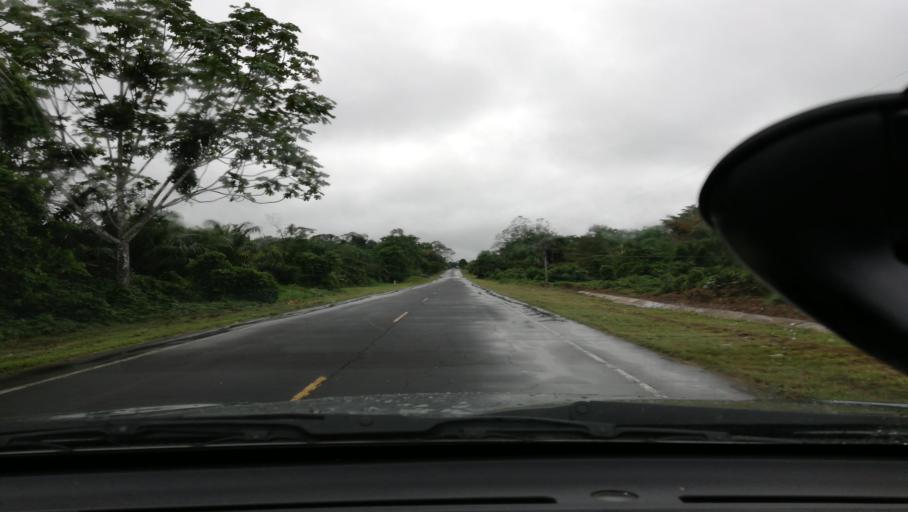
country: PE
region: Loreto
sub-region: Provincia de Maynas
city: San Juan
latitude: -4.1116
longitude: -73.4592
